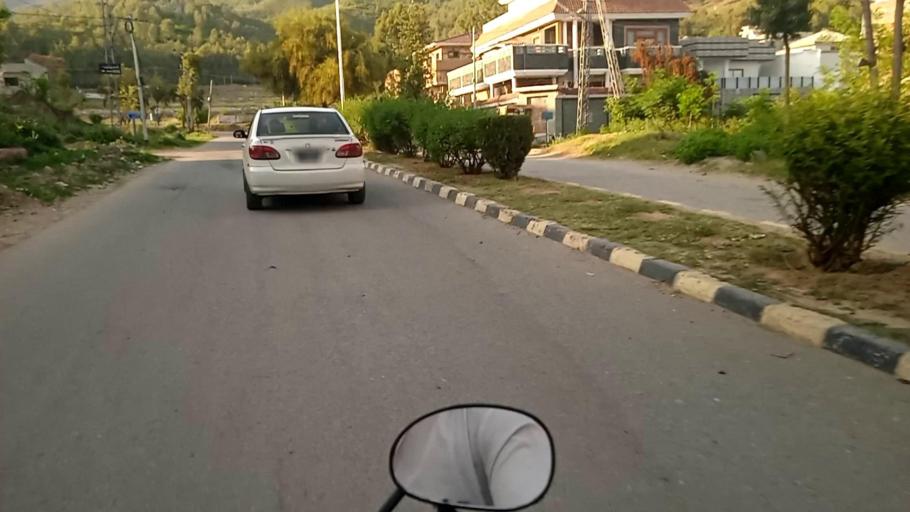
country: PK
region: Khyber Pakhtunkhwa
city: Mingora
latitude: 34.8318
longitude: 72.3421
